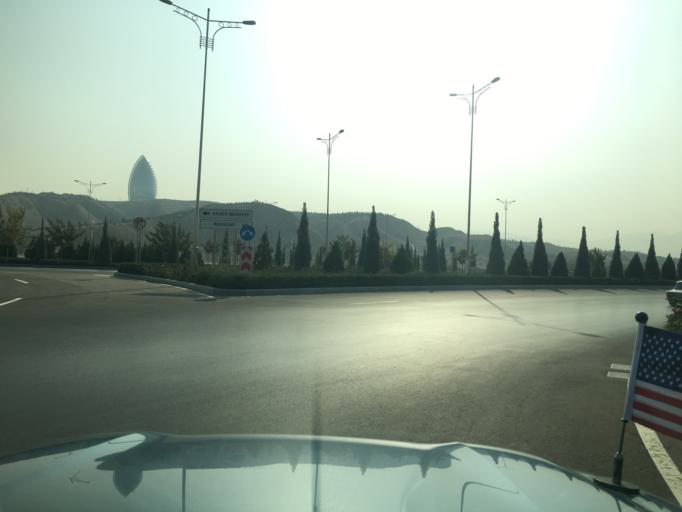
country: TM
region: Ahal
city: Ashgabat
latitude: 37.9363
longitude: 58.3212
